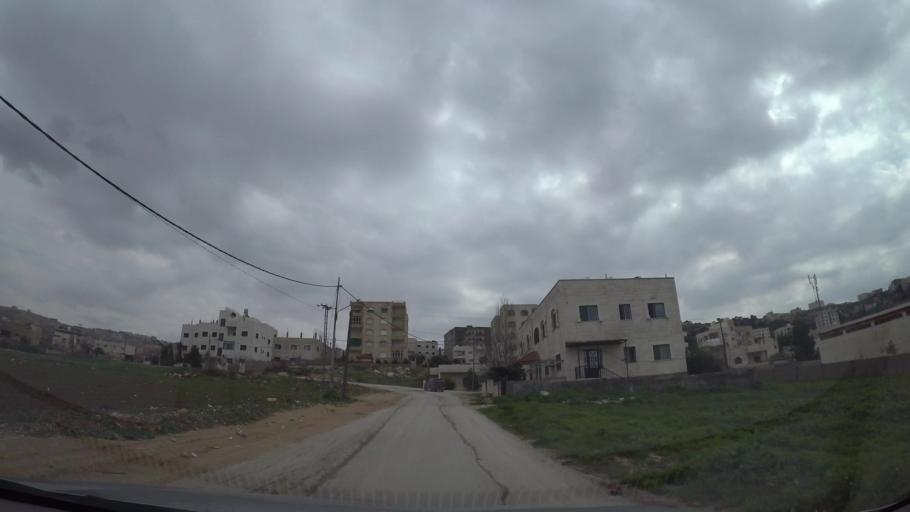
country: JO
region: Amman
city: Al Jubayhah
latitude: 32.0526
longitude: 35.8423
